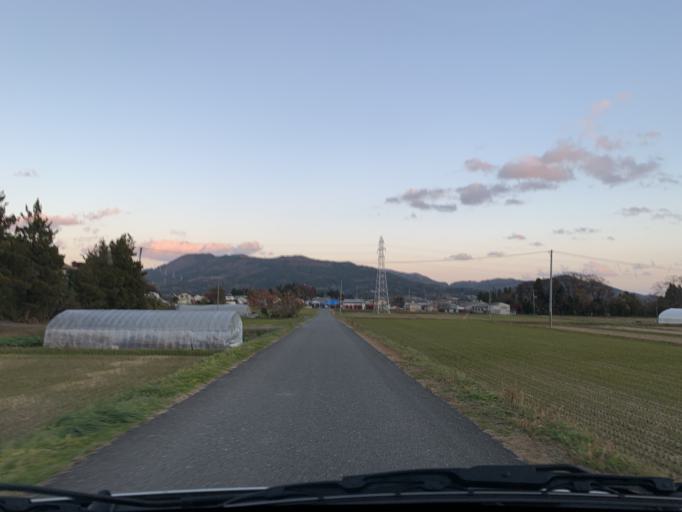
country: JP
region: Iwate
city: Ichinoseki
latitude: 39.0118
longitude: 141.1052
